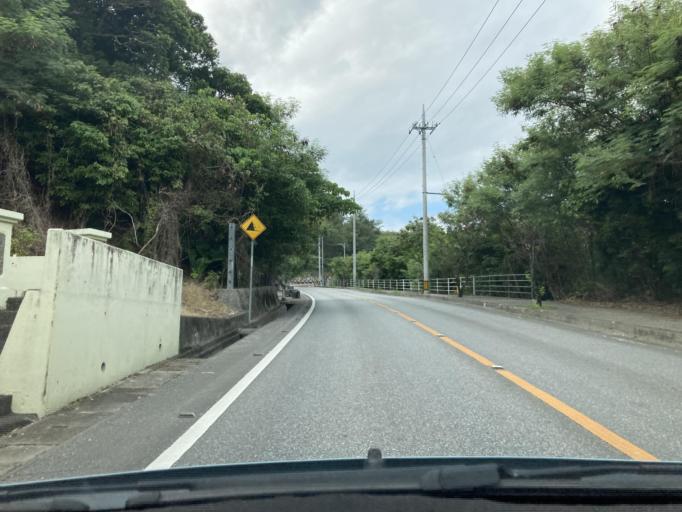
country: JP
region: Okinawa
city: Ginowan
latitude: 26.2604
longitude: 127.7847
